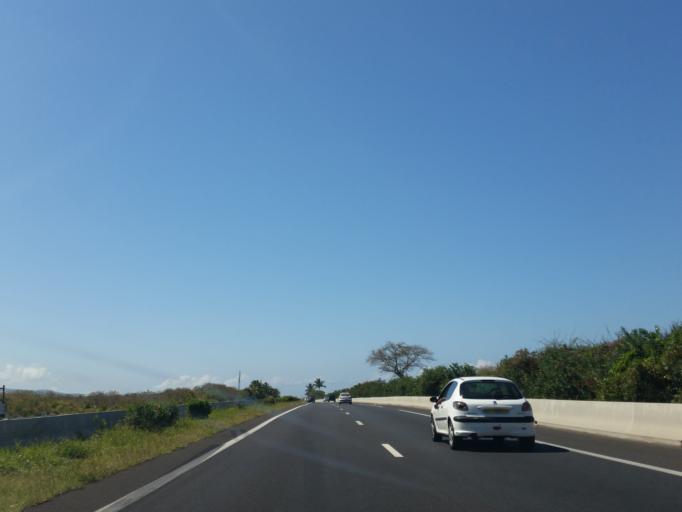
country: RE
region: Reunion
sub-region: Reunion
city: Saint-Louis
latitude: -21.3109
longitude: 55.4350
